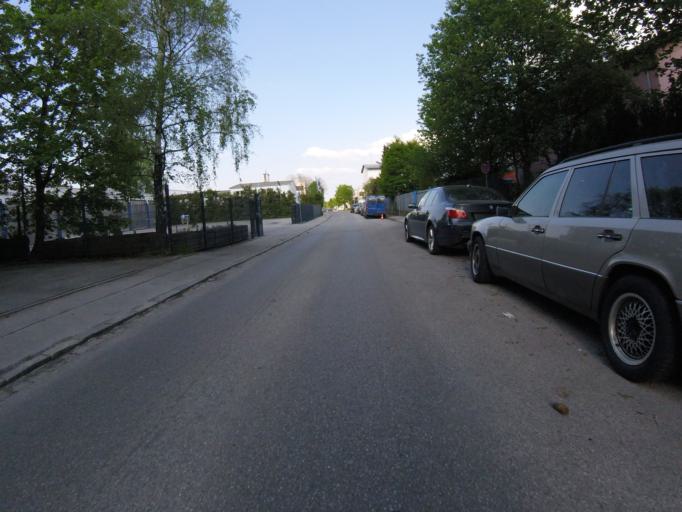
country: DE
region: Bavaria
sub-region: Upper Bavaria
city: Ottobrunn
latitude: 48.0544
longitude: 11.6727
